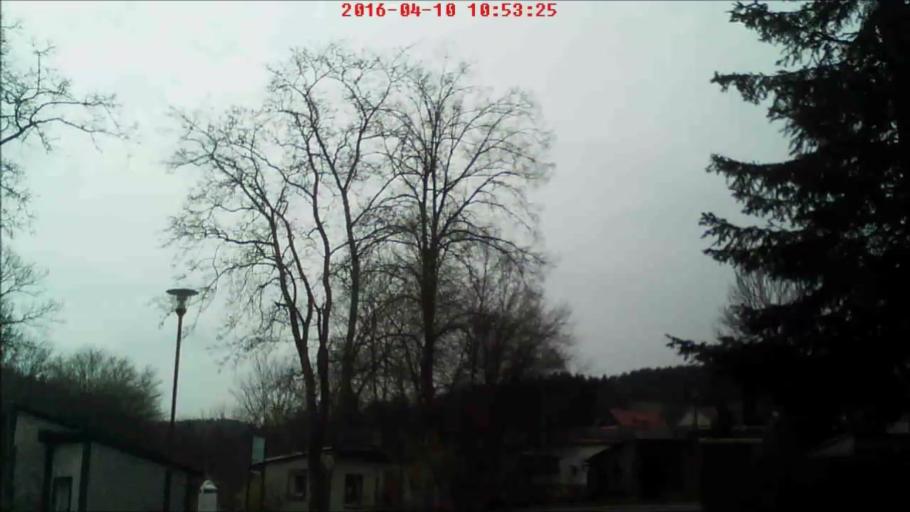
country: DE
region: Thuringia
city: Stutzerbach
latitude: 50.6331
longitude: 10.8617
